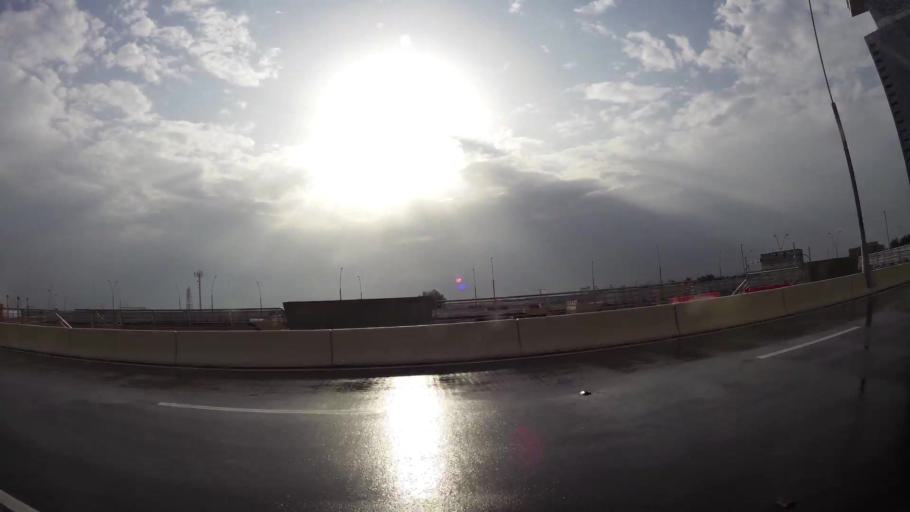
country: AE
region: Abu Dhabi
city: Abu Dhabi
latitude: 24.4967
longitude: 54.4102
